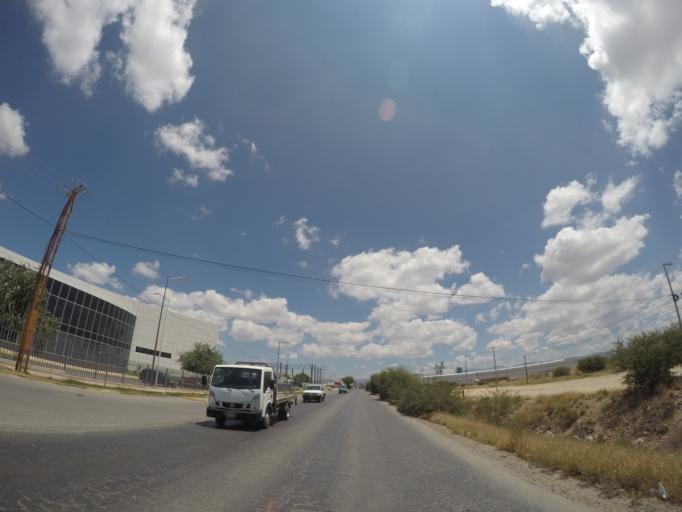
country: MX
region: San Luis Potosi
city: La Pila
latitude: 22.0431
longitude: -100.8829
